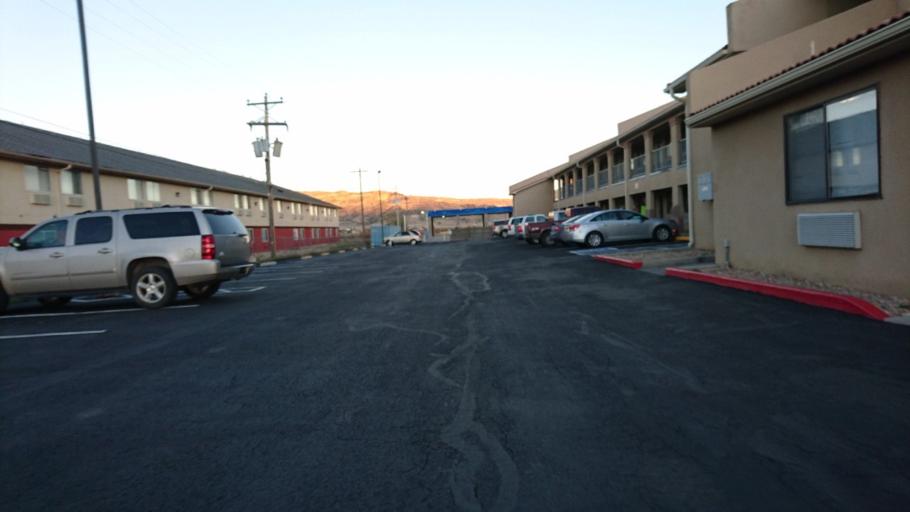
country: US
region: New Mexico
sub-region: Cibola County
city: Grants
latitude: 35.1271
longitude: -107.8272
